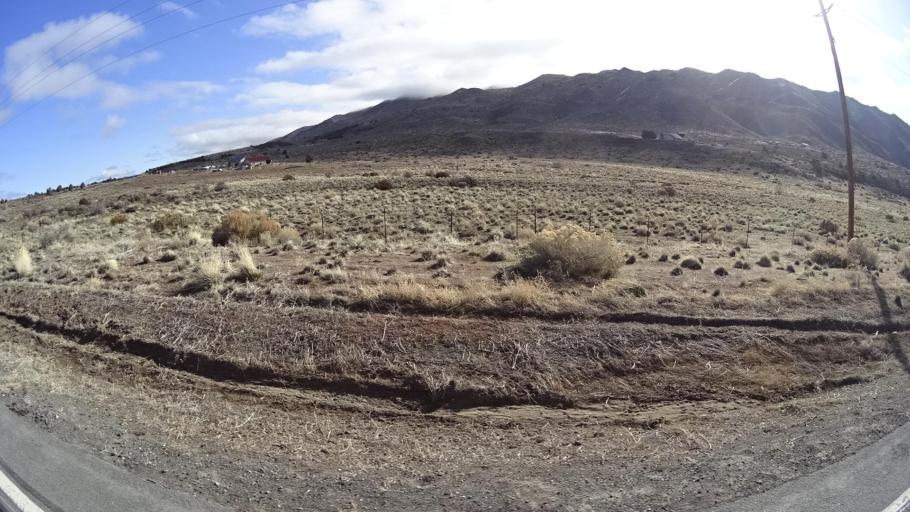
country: US
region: Nevada
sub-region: Washoe County
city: Cold Springs
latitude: 39.7693
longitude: -119.8872
